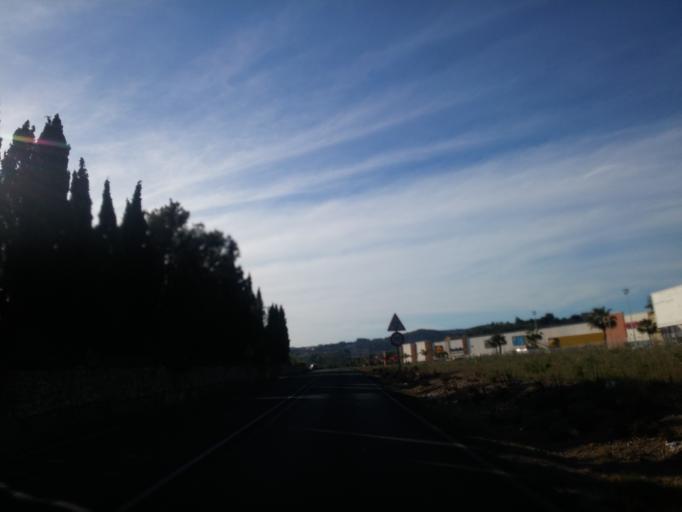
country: ES
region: Valencia
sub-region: Provincia de Alicante
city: Moraira
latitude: 38.7106
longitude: 0.1319
